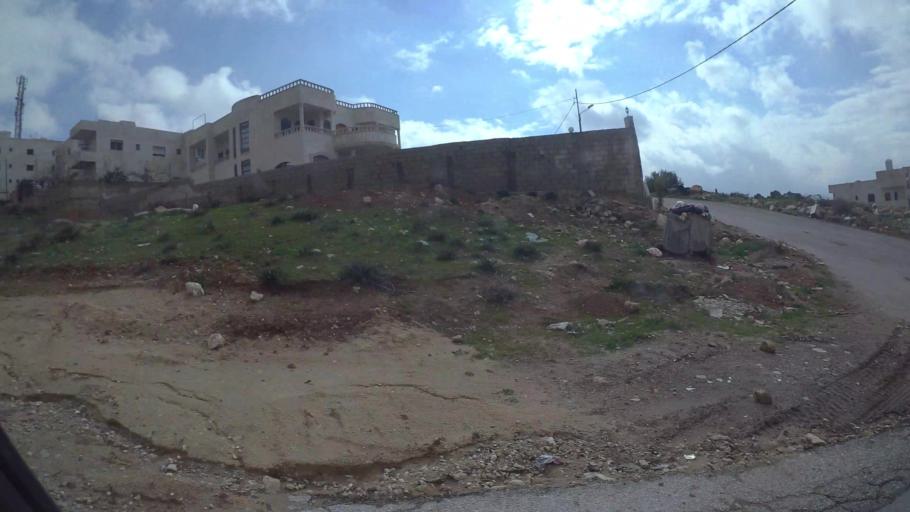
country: JO
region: Amman
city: Al Jubayhah
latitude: 32.0710
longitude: 35.8666
